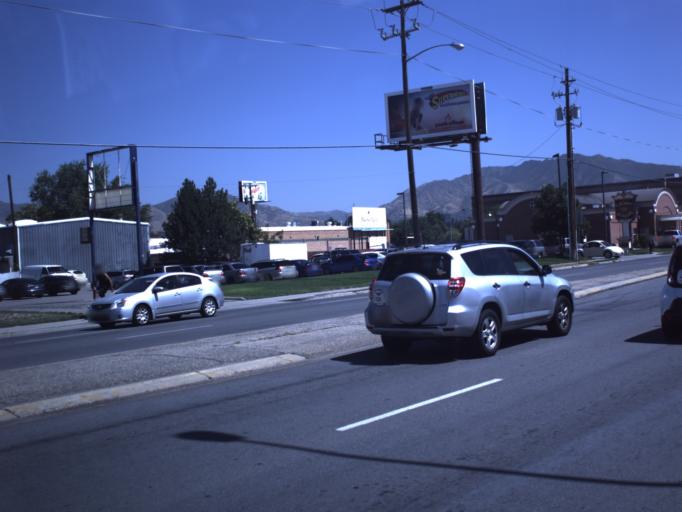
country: US
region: Utah
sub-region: Salt Lake County
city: Centerfield
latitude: 40.6997
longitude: -111.8900
